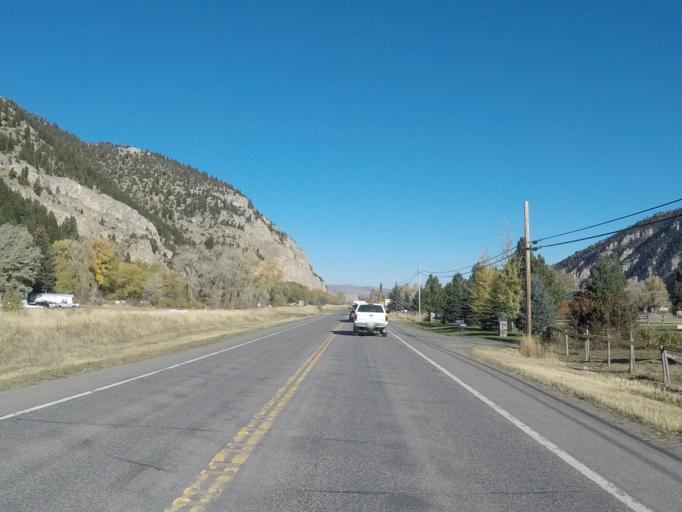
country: US
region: Montana
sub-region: Park County
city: Livingston
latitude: 45.6018
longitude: -110.5736
